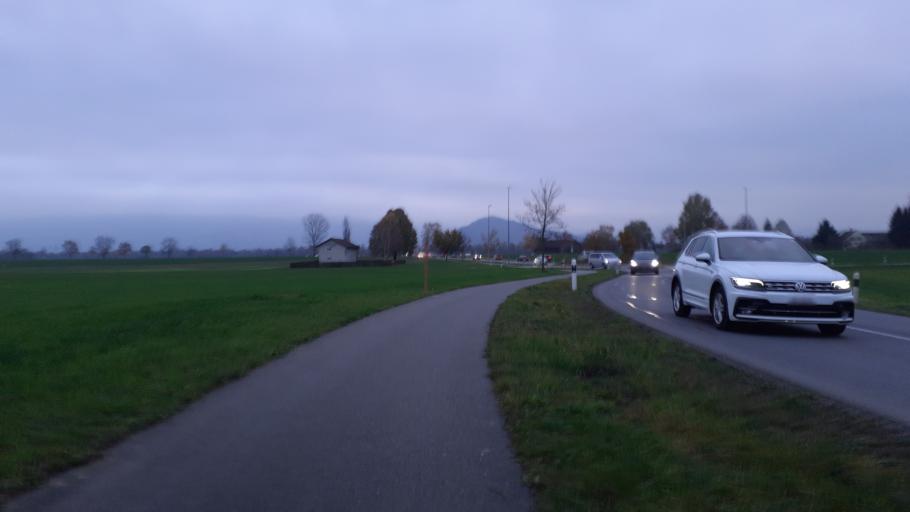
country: CH
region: Saint Gallen
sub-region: Wahlkreis Rheintal
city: Altstatten
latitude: 47.3729
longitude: 9.5645
